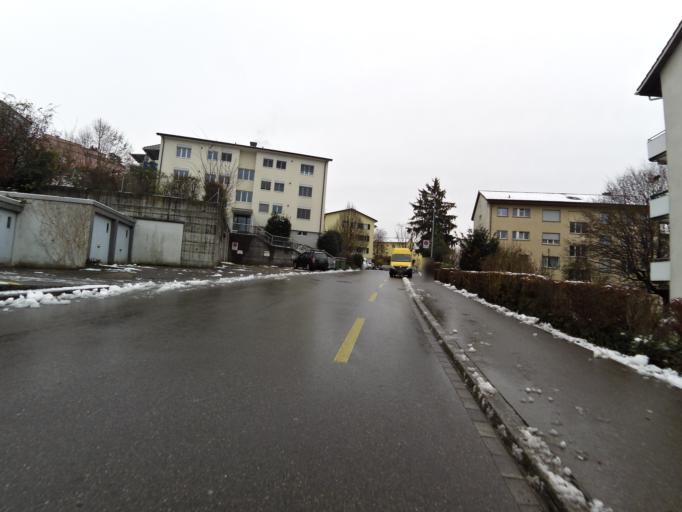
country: CH
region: Thurgau
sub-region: Frauenfeld District
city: Frauenfeld
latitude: 47.5625
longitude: 8.9094
